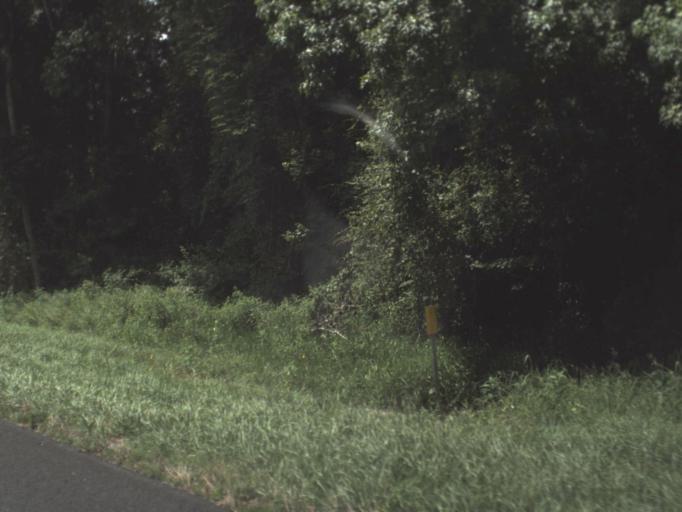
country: US
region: Florida
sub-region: Taylor County
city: Perry
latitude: 30.2841
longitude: -83.7308
